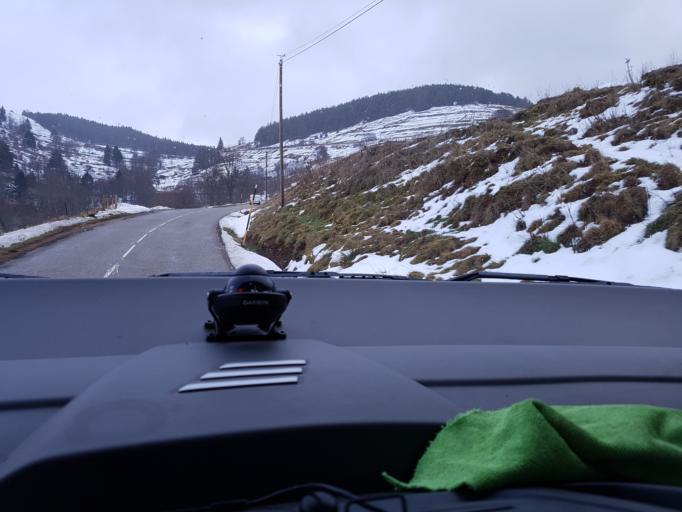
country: FR
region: Alsace
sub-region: Departement du Haut-Rhin
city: Soultzeren
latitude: 48.0802
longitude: 7.1088
